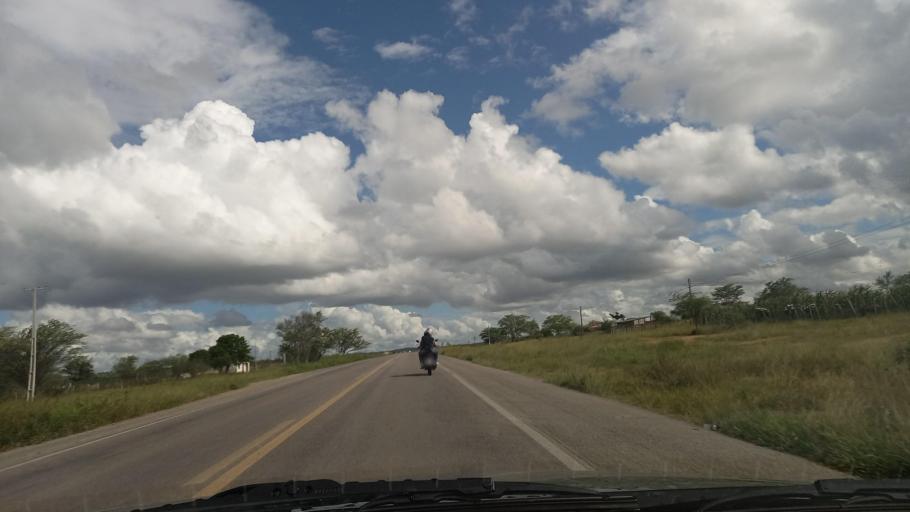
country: BR
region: Pernambuco
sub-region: Lajedo
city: Lajedo
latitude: -8.6167
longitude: -36.2991
